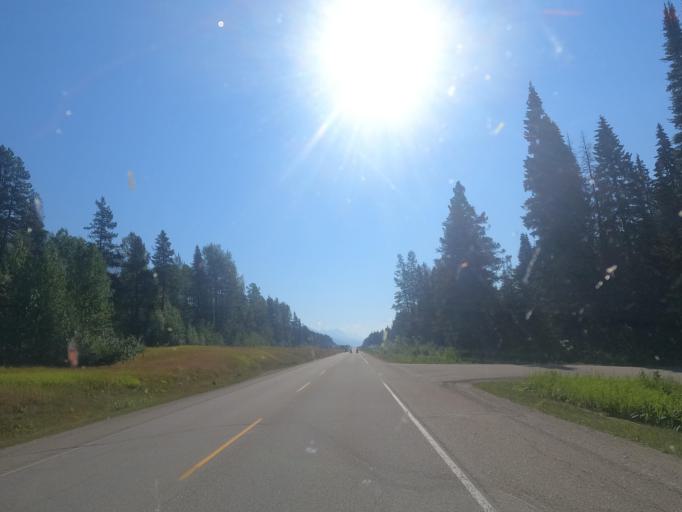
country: CA
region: Alberta
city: Grande Cache
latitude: 52.9880
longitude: -119.0023
